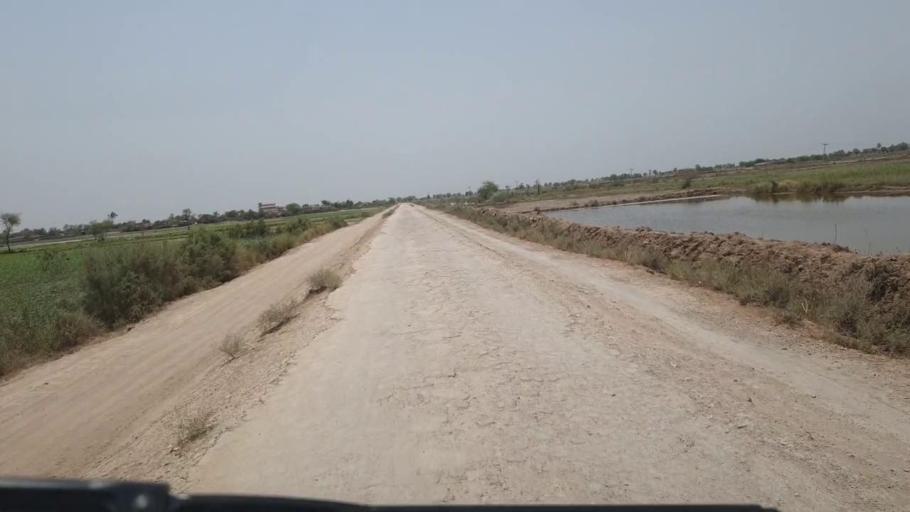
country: PK
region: Sindh
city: Daur
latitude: 26.4613
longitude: 68.1453
